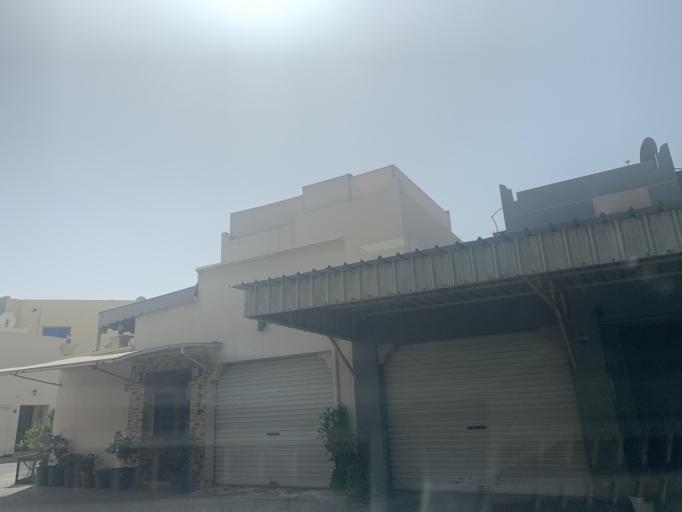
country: BH
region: Northern
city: Sitrah
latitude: 26.1686
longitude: 50.6143
